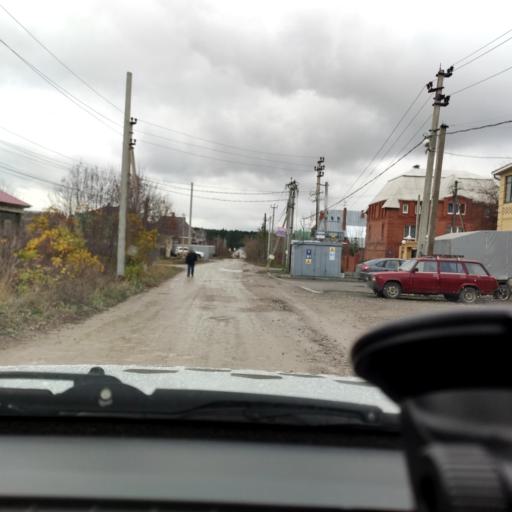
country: RU
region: Perm
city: Perm
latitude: 57.9898
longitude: 56.3054
